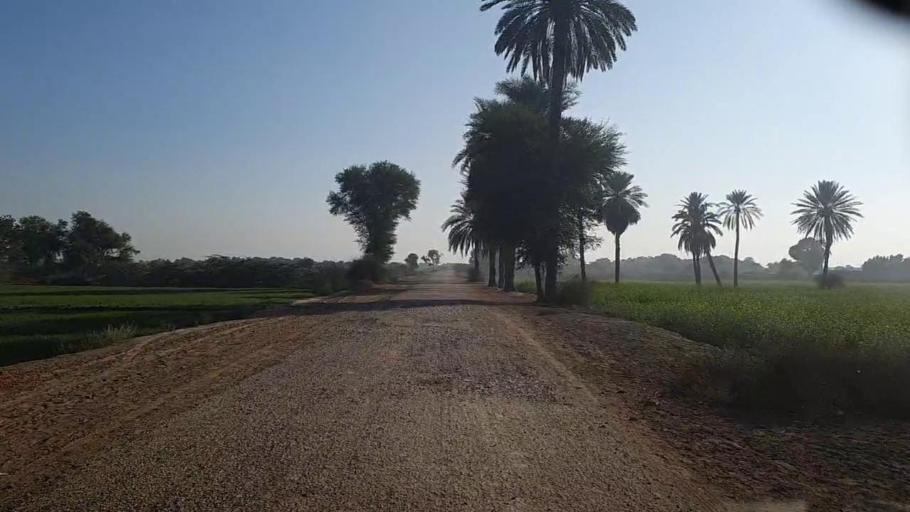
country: PK
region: Sindh
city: Darya Khan Marri
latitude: 26.6941
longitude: 68.3625
